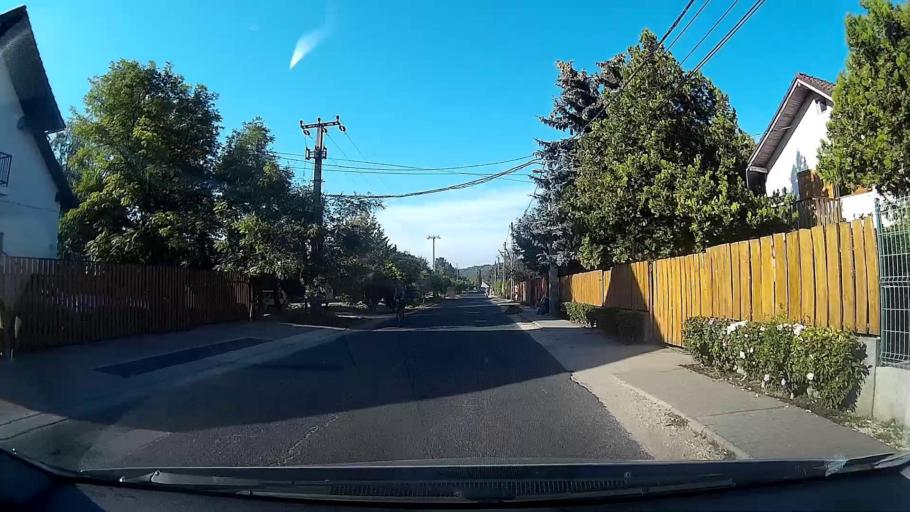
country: HU
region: Pest
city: Budakalasz
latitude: 47.6198
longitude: 19.0596
